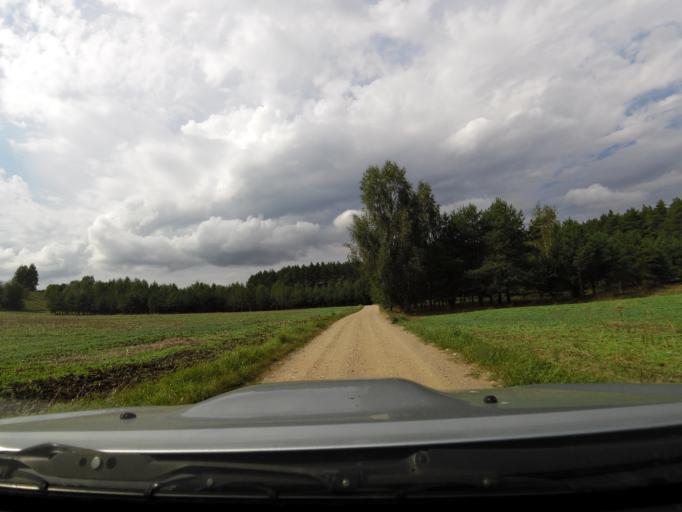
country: LT
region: Vilnius County
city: Elektrenai
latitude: 54.9197
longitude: 24.7447
